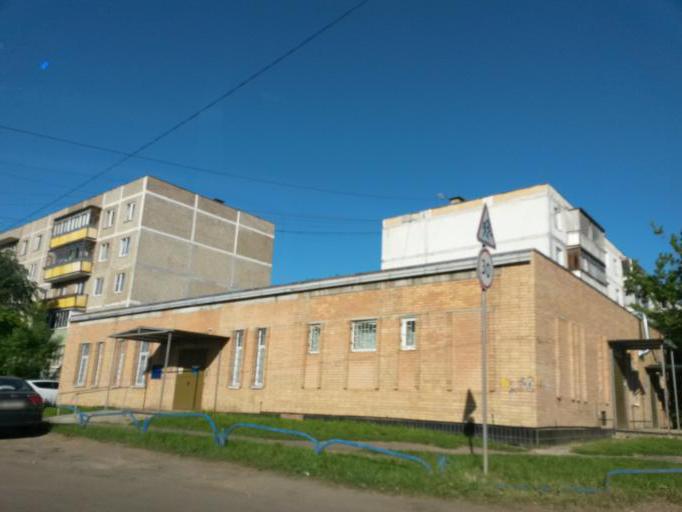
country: RU
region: Moskovskaya
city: Lyubuchany
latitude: 55.2393
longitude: 37.5393
